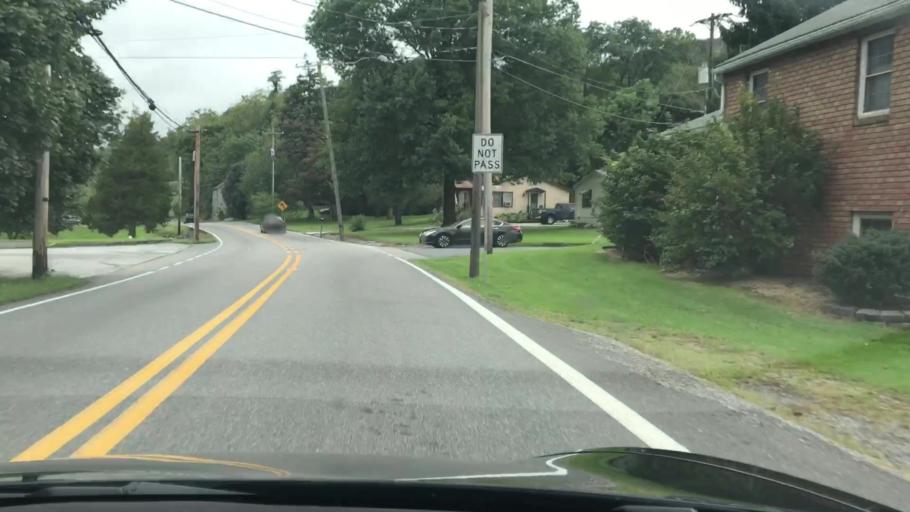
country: US
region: Pennsylvania
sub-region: York County
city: Dillsburg
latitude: 40.1030
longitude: -77.0592
